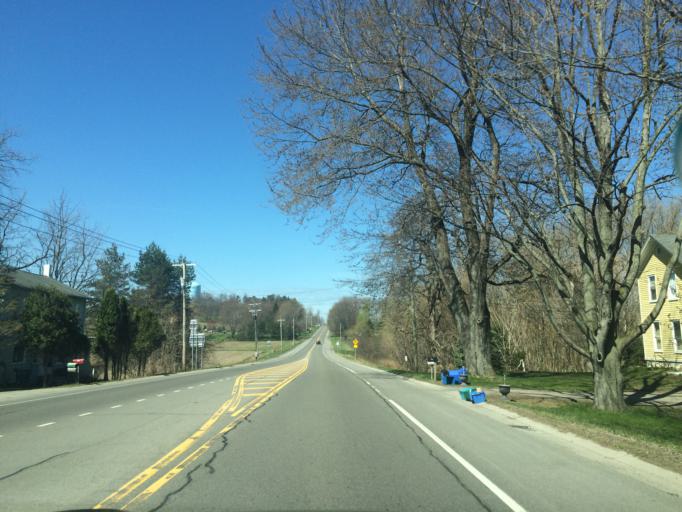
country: US
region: New York
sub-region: Wayne County
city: Macedon
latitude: 43.0942
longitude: -77.3027
